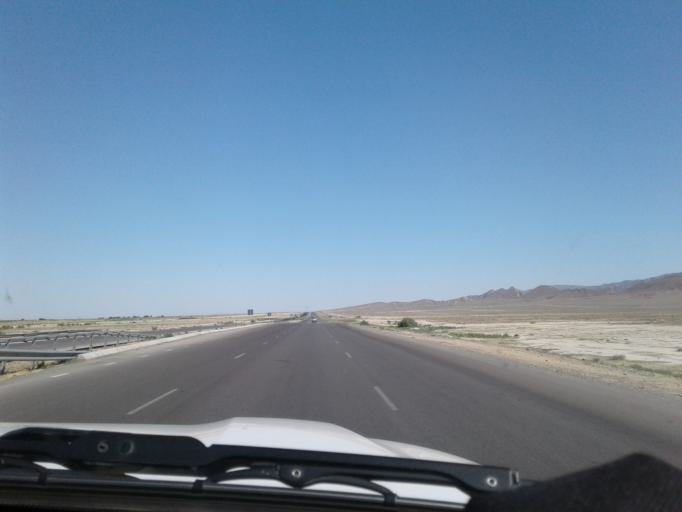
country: IR
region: Razavi Khorasan
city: Dargaz
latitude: 37.7167
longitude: 59.0161
